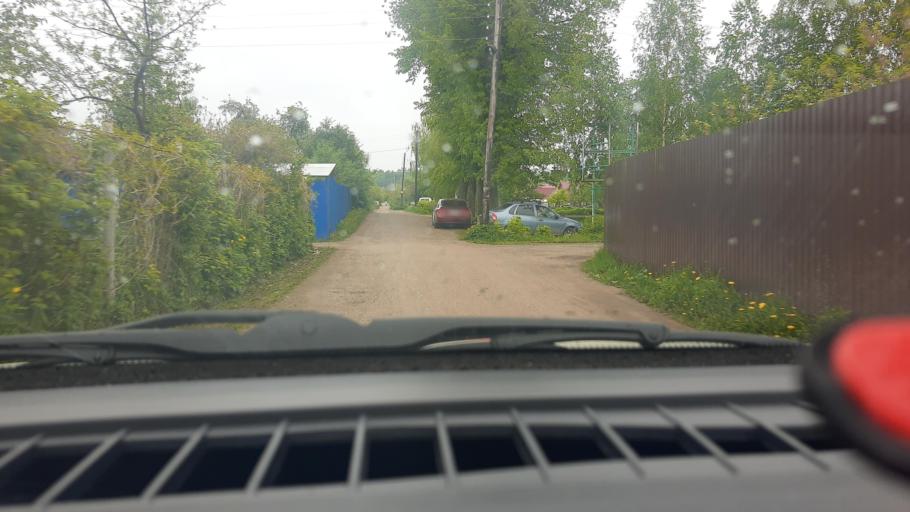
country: RU
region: Nizjnij Novgorod
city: Burevestnik
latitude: 56.2171
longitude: 43.8508
